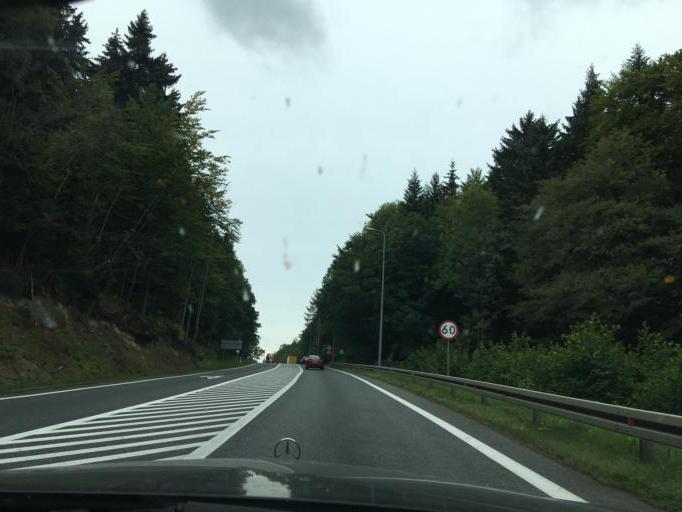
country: PL
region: Lower Silesian Voivodeship
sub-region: Powiat klodzki
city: Duszniki-Zdroj
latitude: 50.3970
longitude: 16.3525
